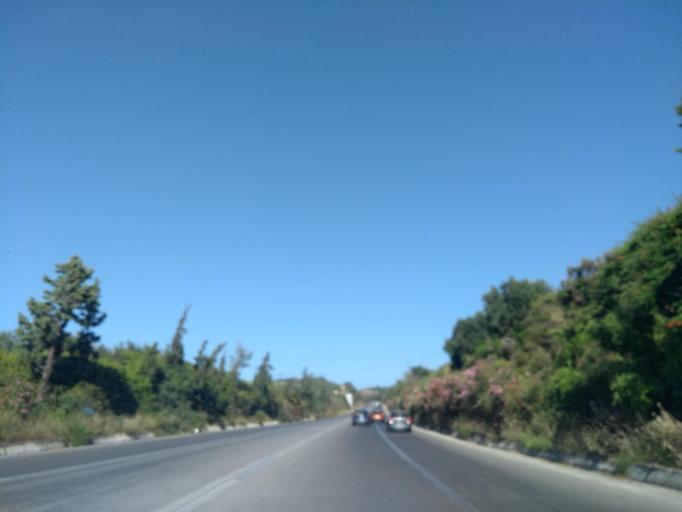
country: GR
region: Crete
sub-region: Nomos Chanias
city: Agia Marina
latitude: 35.5128
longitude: 23.9016
